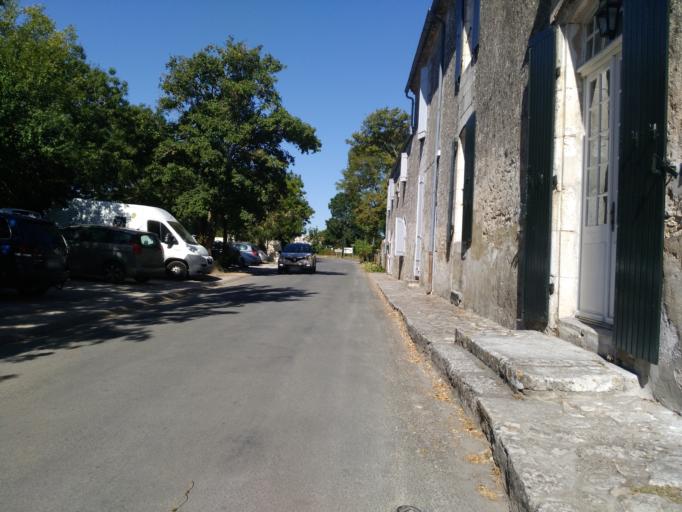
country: FR
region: Poitou-Charentes
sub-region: Departement de la Charente-Maritime
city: Breuillet
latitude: 45.7103
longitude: -1.0313
